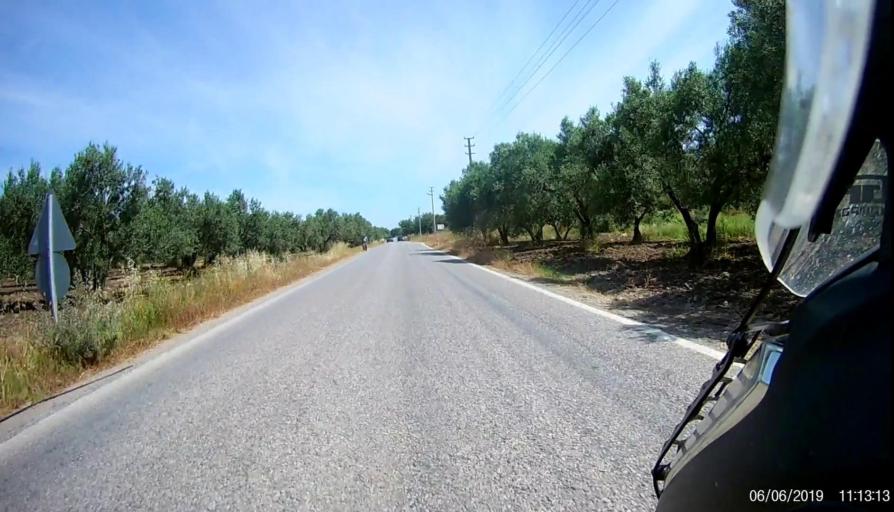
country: TR
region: Canakkale
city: Gulpinar
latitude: 39.6128
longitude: 26.1791
